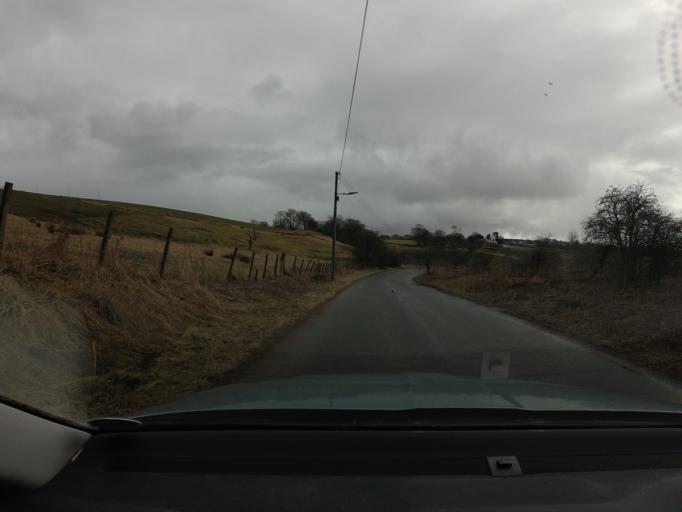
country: GB
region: Scotland
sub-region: South Lanarkshire
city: Lanark
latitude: 55.6030
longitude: -3.7863
